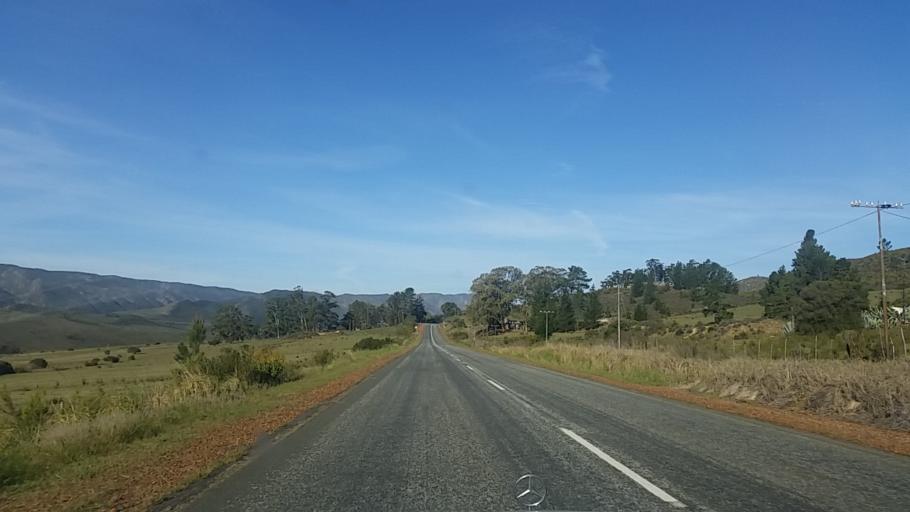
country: ZA
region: Western Cape
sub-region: Eden District Municipality
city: Knysna
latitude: -33.7740
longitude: 22.9129
